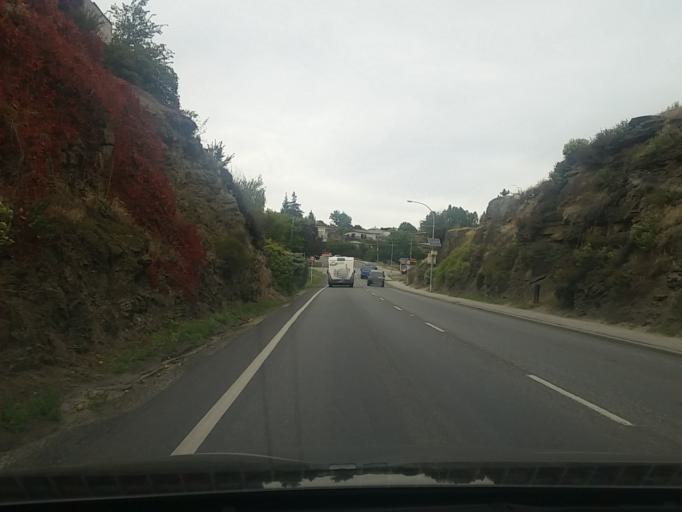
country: NZ
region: Otago
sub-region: Queenstown-Lakes District
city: Wanaka
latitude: -45.2597
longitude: 169.3894
